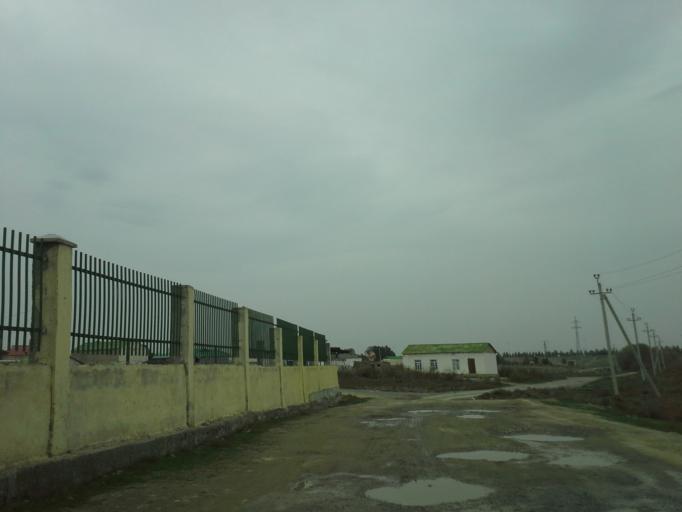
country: TM
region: Ahal
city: Abadan
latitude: 37.9787
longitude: 58.2266
